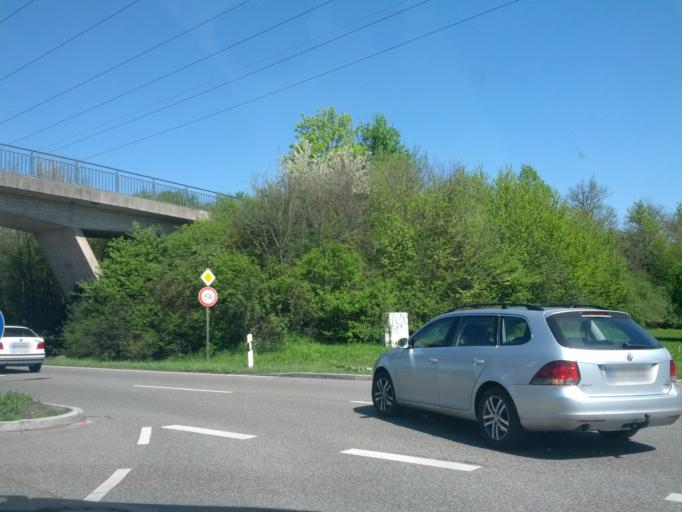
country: DE
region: Baden-Wuerttemberg
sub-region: Freiburg Region
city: Umkirch
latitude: 48.0000
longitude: 7.7987
